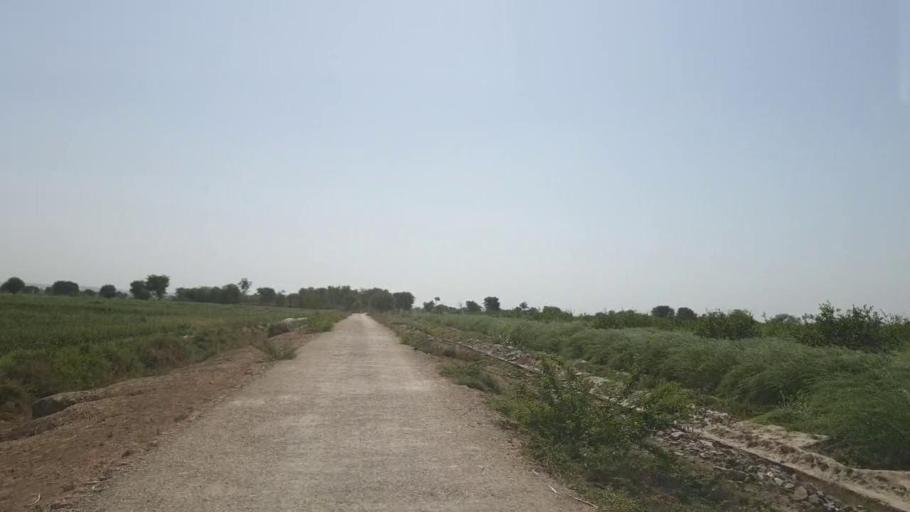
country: PK
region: Sindh
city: Naukot
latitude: 24.9074
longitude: 69.4777
